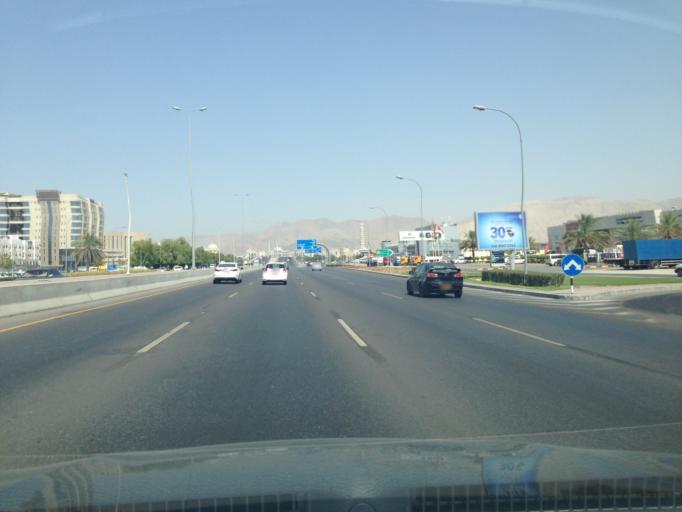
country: OM
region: Muhafazat Masqat
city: Bawshar
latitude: 23.5900
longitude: 58.3767
